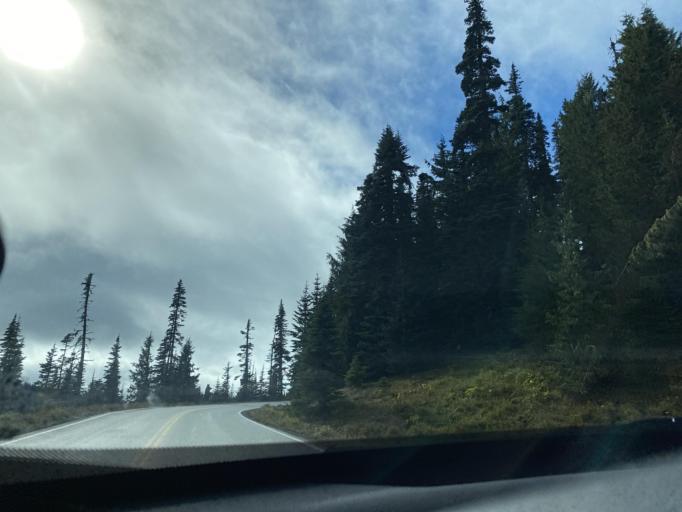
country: US
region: Washington
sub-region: Clallam County
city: Port Angeles
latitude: 47.9797
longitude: -123.4720
